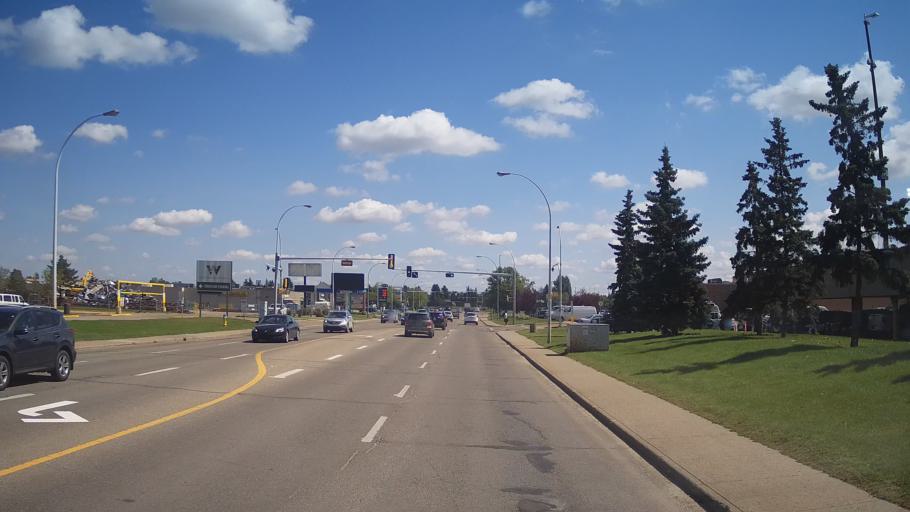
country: CA
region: Alberta
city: St. Albert
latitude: 53.5248
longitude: -113.6219
